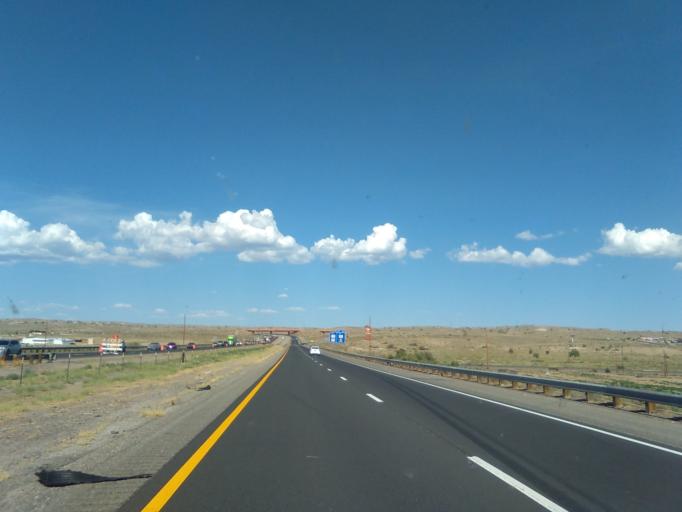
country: US
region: New Mexico
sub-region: Bernalillo County
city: South Valley
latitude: 34.9506
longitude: -106.6767
